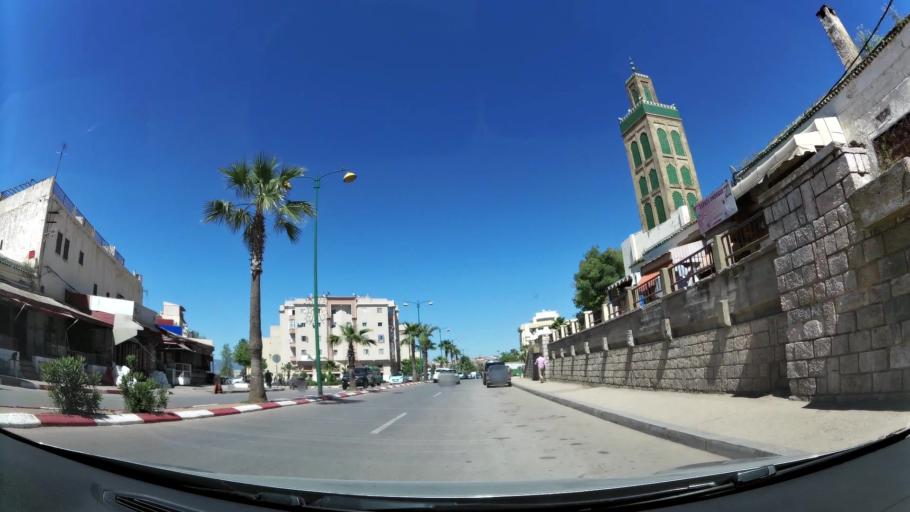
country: MA
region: Meknes-Tafilalet
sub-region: Meknes
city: Meknes
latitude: 33.8902
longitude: -5.5787
